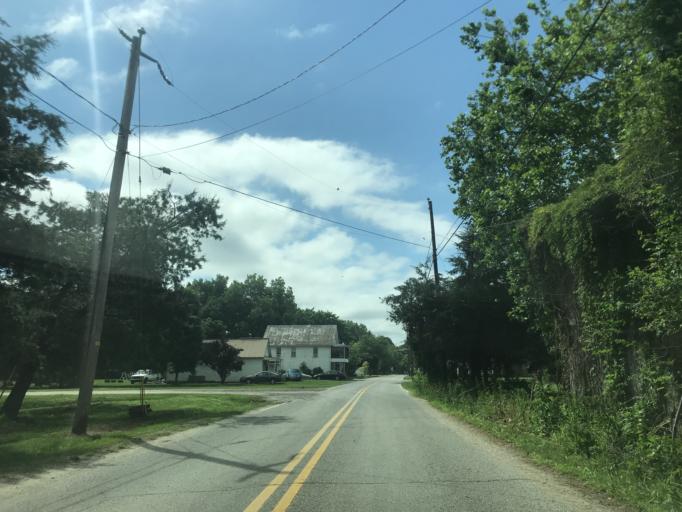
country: US
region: Maryland
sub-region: Caroline County
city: Ridgely
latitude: 38.9212
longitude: -75.9559
